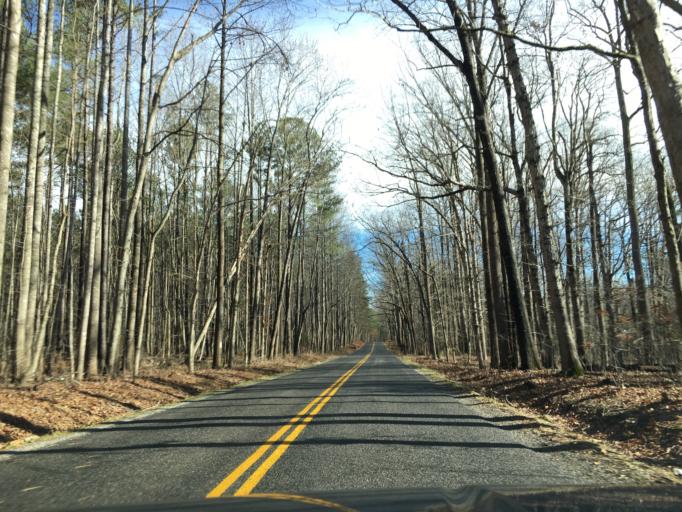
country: US
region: Virginia
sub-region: Amelia County
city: Amelia Court House
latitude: 37.4365
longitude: -78.0397
